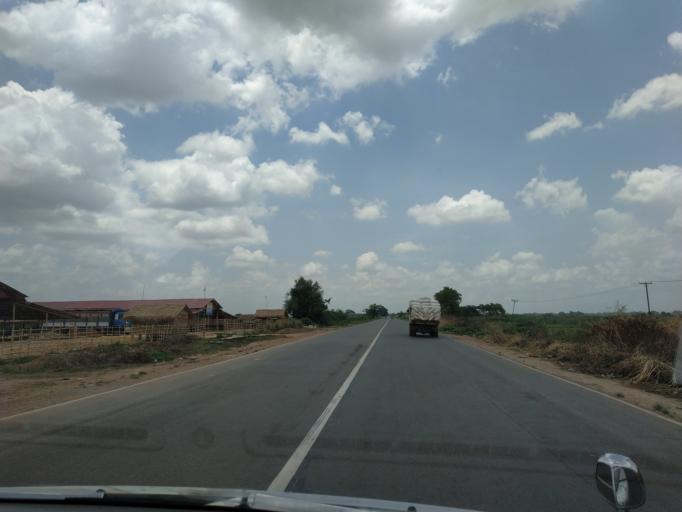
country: MM
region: Bago
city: Bago
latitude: 17.4707
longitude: 96.5538
